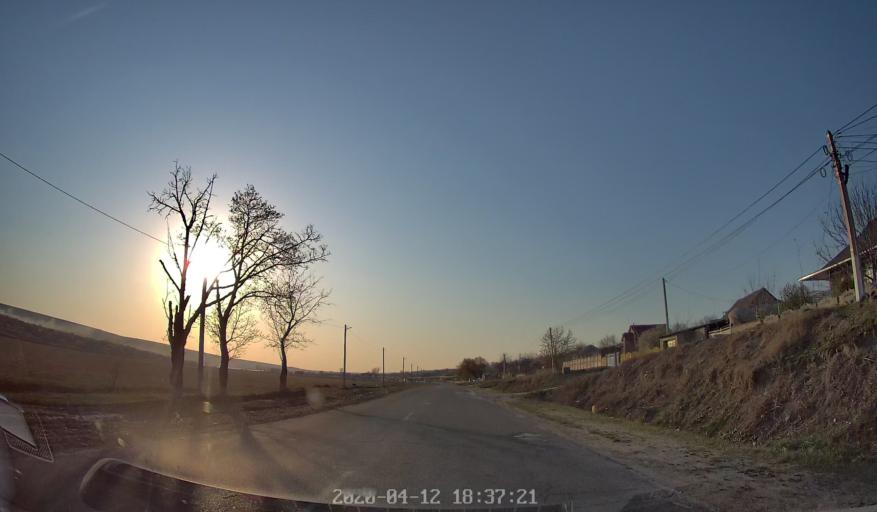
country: MD
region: Chisinau
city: Vadul lui Voda
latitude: 47.1204
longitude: 29.0166
